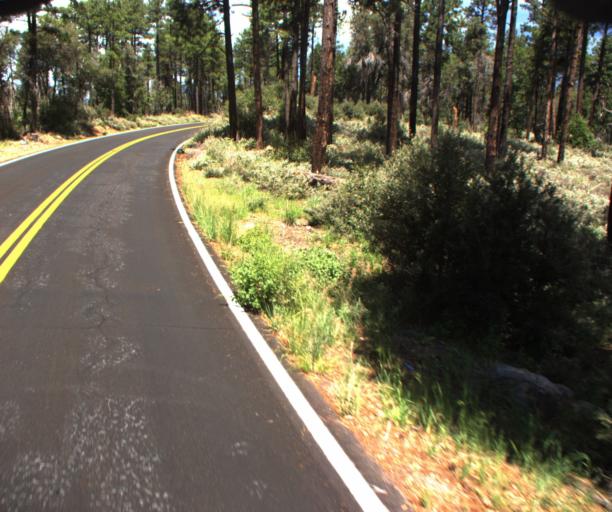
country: US
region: Arizona
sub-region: Greenlee County
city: Morenci
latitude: 33.4728
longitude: -109.3742
